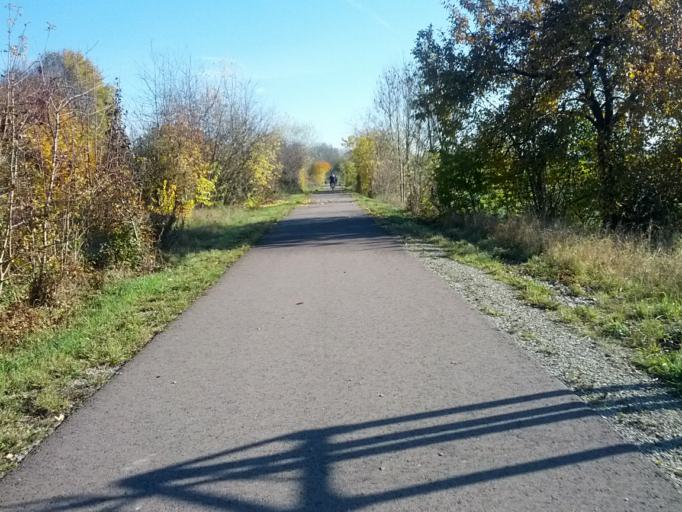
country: DE
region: Thuringia
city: Friedrichswerth
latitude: 50.9963
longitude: 10.5498
